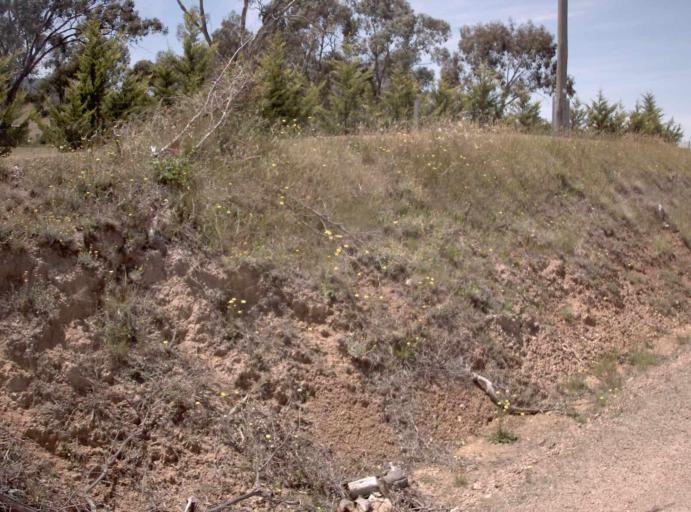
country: AU
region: Victoria
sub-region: Alpine
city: Mount Beauty
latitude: -37.1014
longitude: 147.6014
